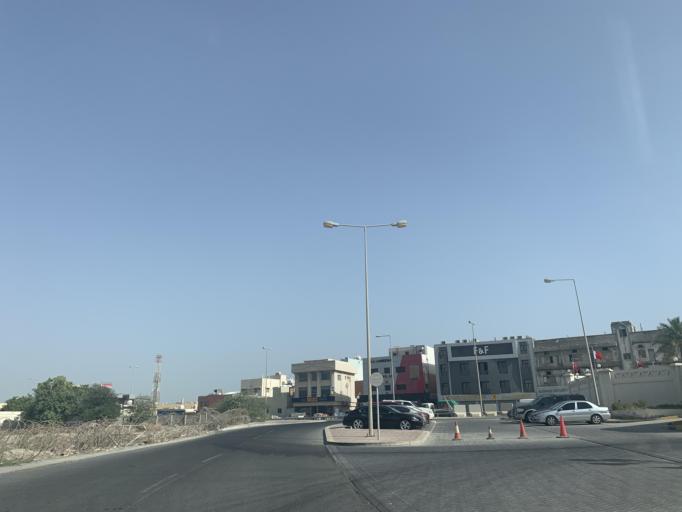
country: BH
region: Manama
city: Jidd Hafs
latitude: 26.2070
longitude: 50.5471
